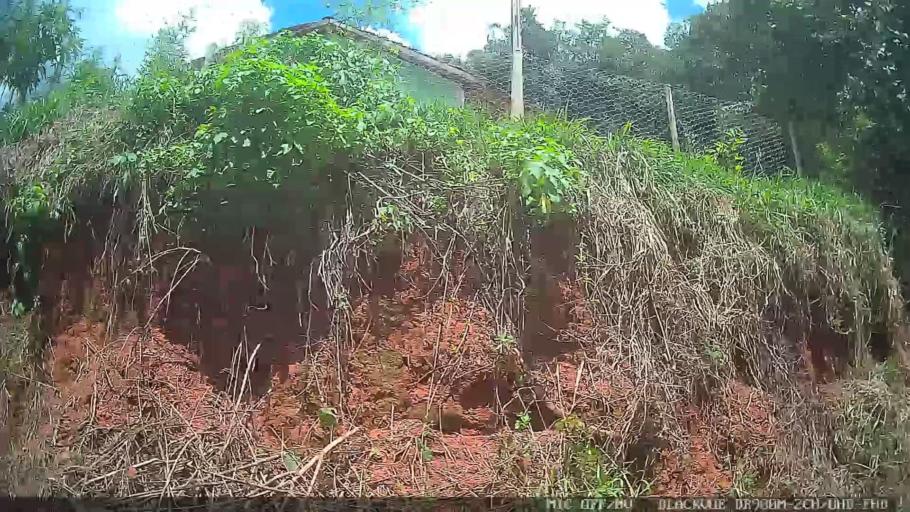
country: BR
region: Minas Gerais
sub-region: Extrema
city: Extrema
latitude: -22.8673
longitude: -46.2874
